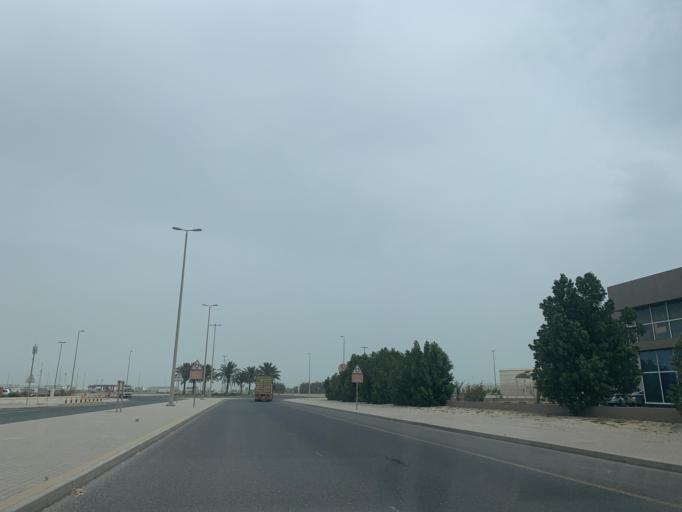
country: BH
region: Muharraq
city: Al Hadd
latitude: 26.2196
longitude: 50.6795
